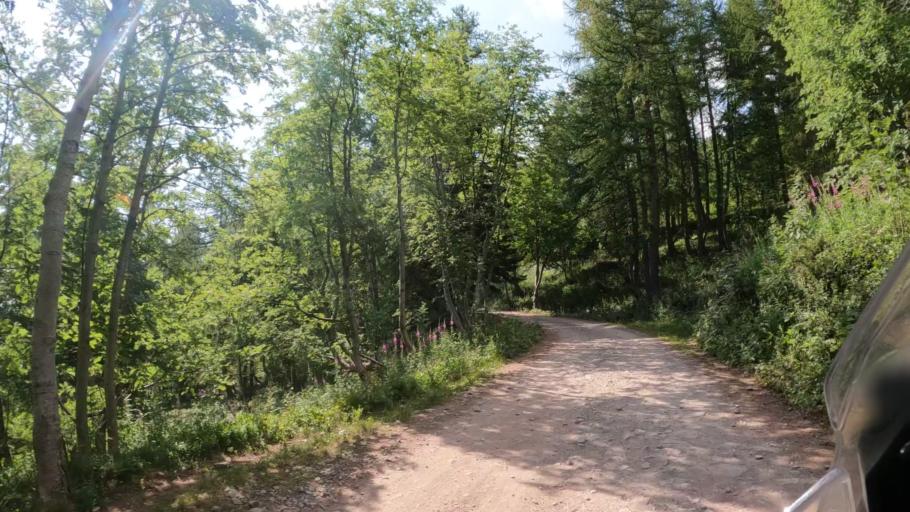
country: IT
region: Piedmont
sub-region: Provincia di Cuneo
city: Briga Alta
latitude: 44.1145
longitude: 7.7015
